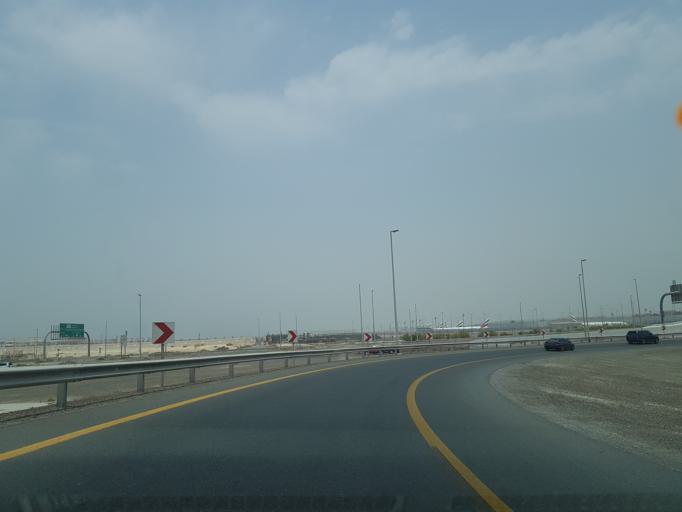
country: AE
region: Ash Shariqah
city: Sharjah
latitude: 25.2330
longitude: 55.4022
